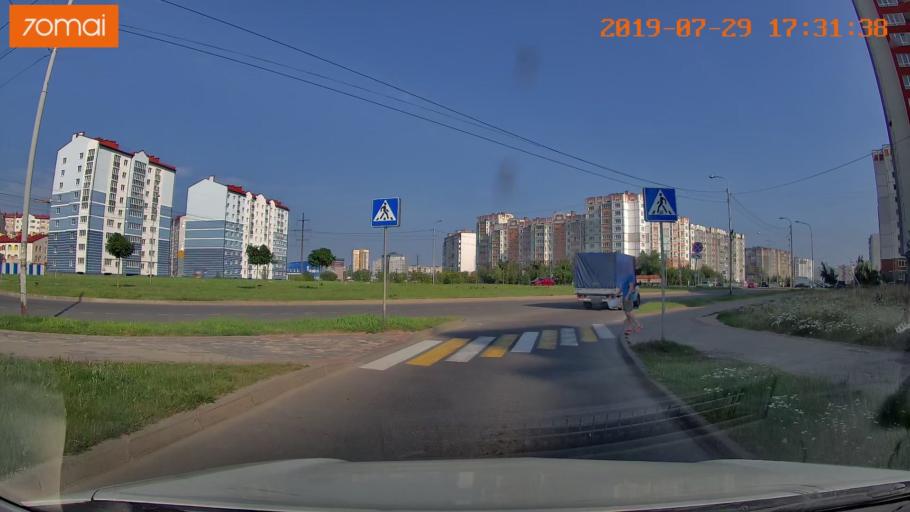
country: RU
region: Kaliningrad
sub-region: Gorod Kaliningrad
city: Kaliningrad
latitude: 54.7467
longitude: 20.4887
